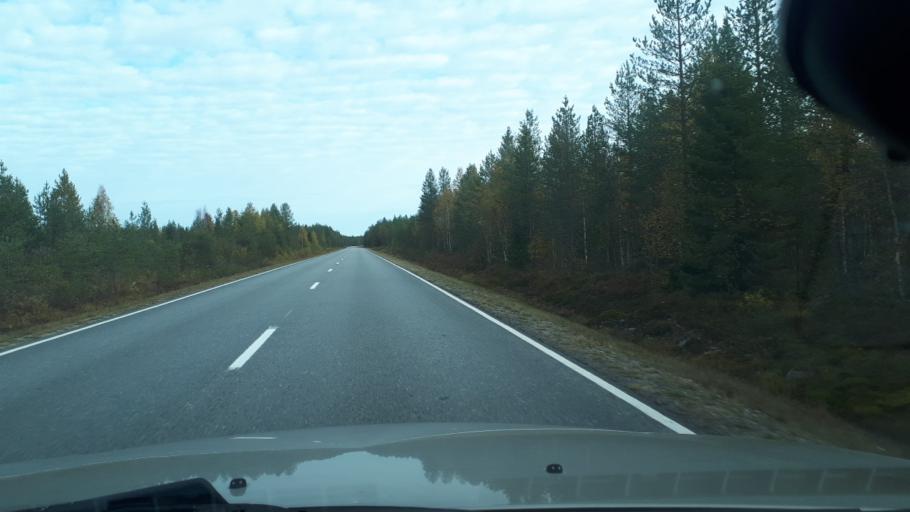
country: FI
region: Northern Ostrobothnia
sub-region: Oulu
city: Yli-Ii
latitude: 65.9042
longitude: 25.7359
